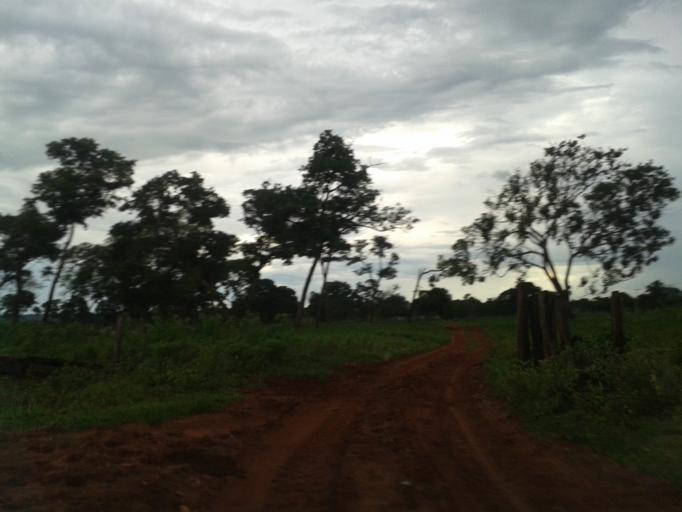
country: BR
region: Minas Gerais
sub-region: Santa Vitoria
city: Santa Vitoria
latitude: -19.1980
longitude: -50.5150
